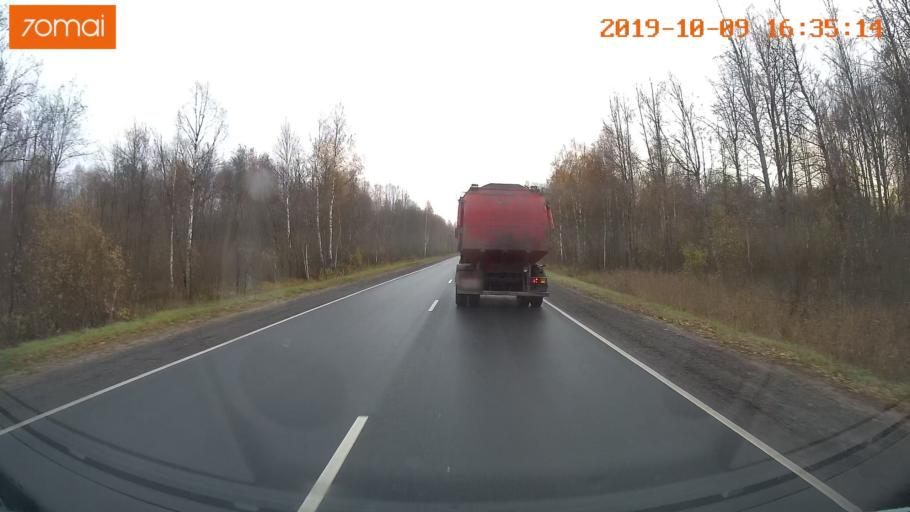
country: RU
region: Kostroma
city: Oktyabr'skiy
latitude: 57.5580
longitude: 40.9989
